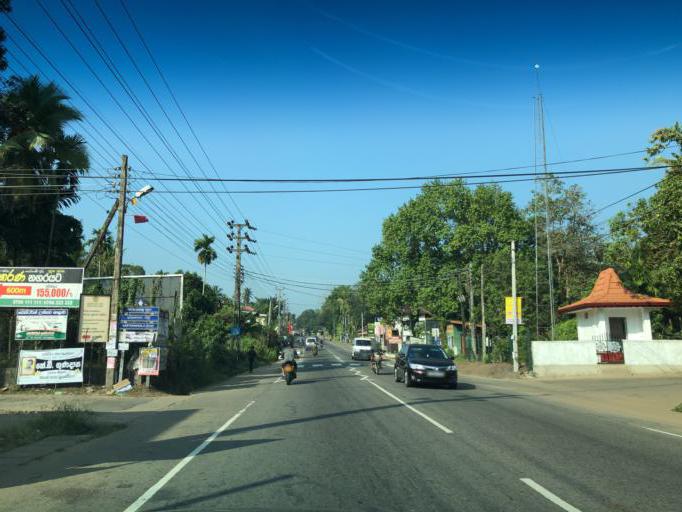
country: LK
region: Western
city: Horana South
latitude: 6.7215
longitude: 80.0753
